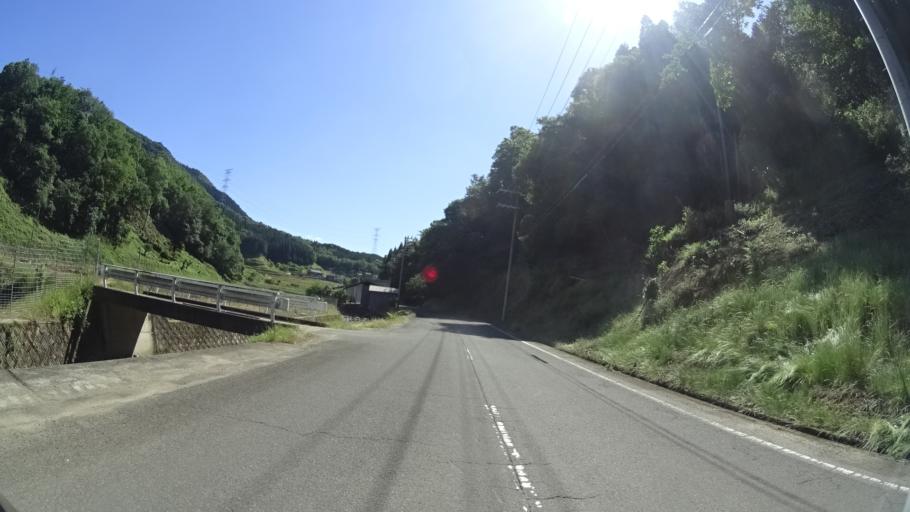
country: JP
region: Kyoto
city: Fukuchiyama
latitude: 35.3586
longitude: 135.0980
